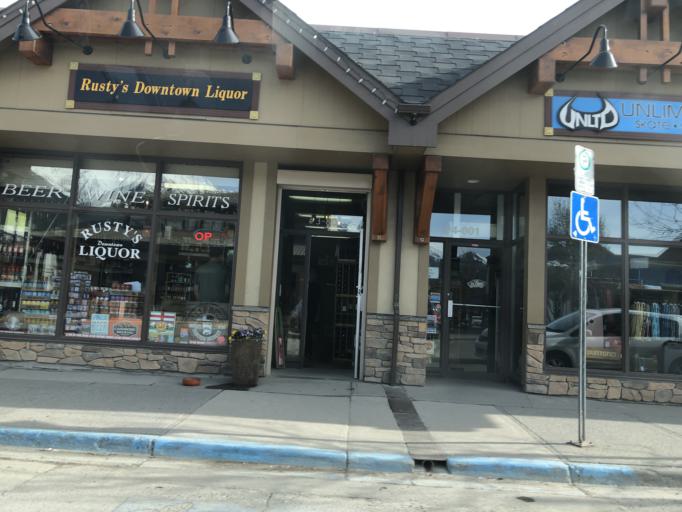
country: CA
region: Alberta
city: Canmore
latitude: 51.0892
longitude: -115.3613
